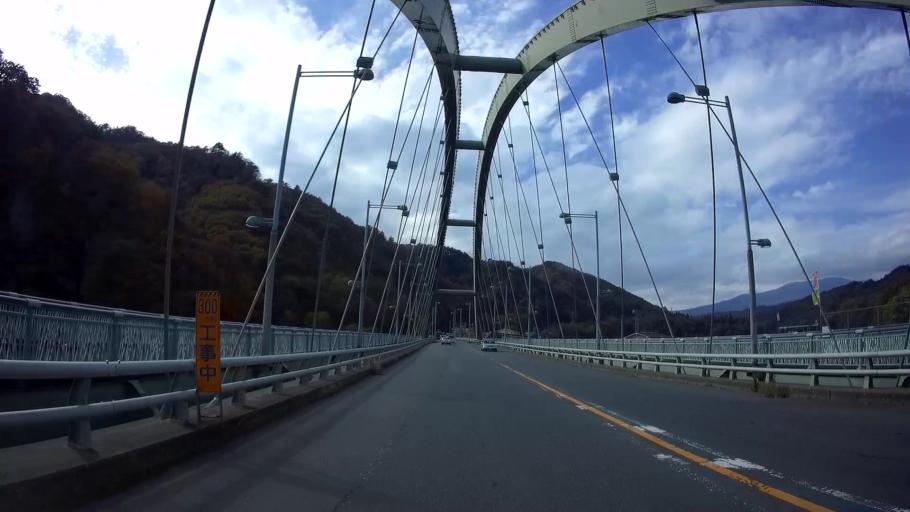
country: JP
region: Gunma
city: Nakanojomachi
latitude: 36.5436
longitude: 138.6537
